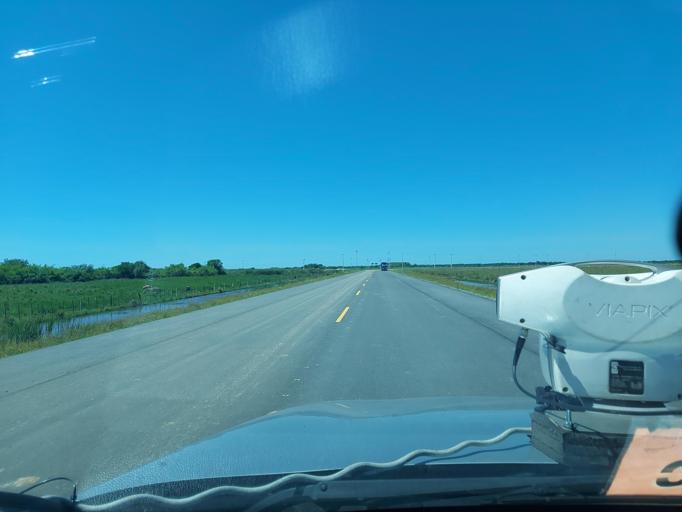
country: PY
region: Neembucu
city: Pilar
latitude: -26.8460
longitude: -58.2308
